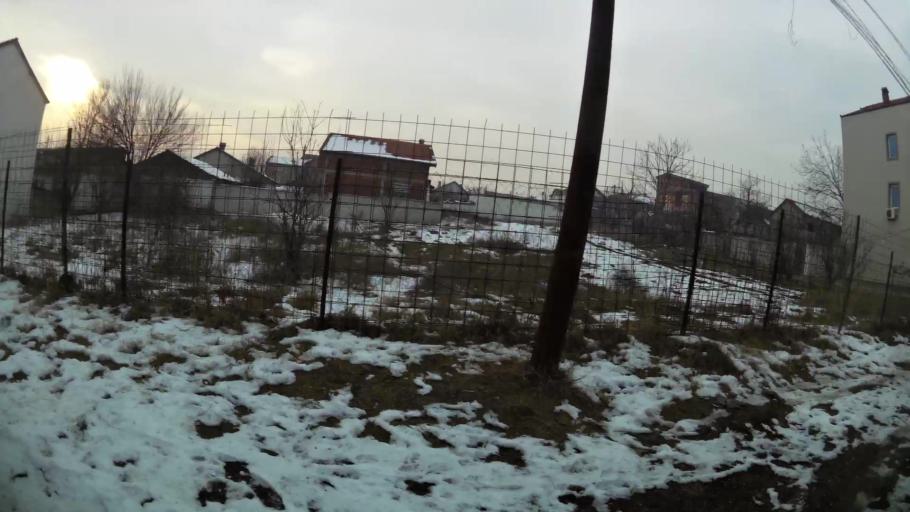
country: MK
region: Butel
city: Butel
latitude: 42.0286
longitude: 21.4342
